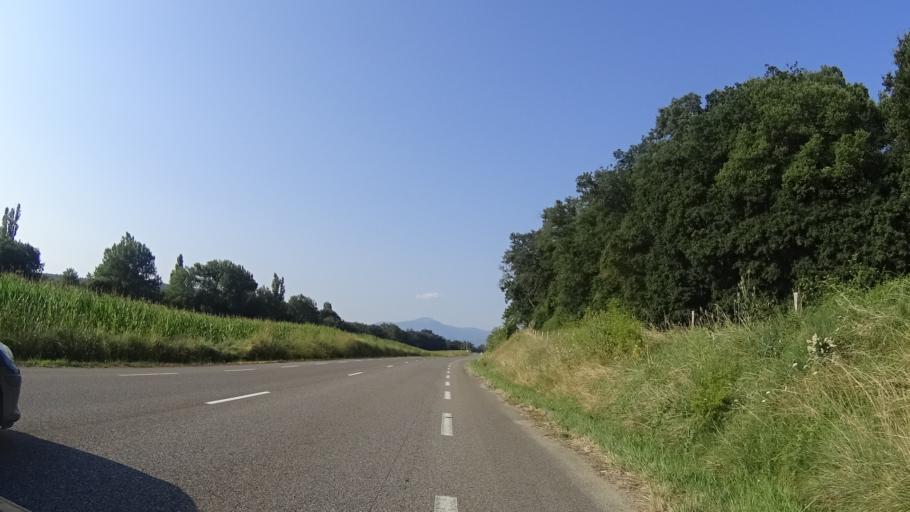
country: FR
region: Midi-Pyrenees
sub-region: Departement de l'Ariege
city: Mirepoix
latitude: 43.0214
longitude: 1.8929
